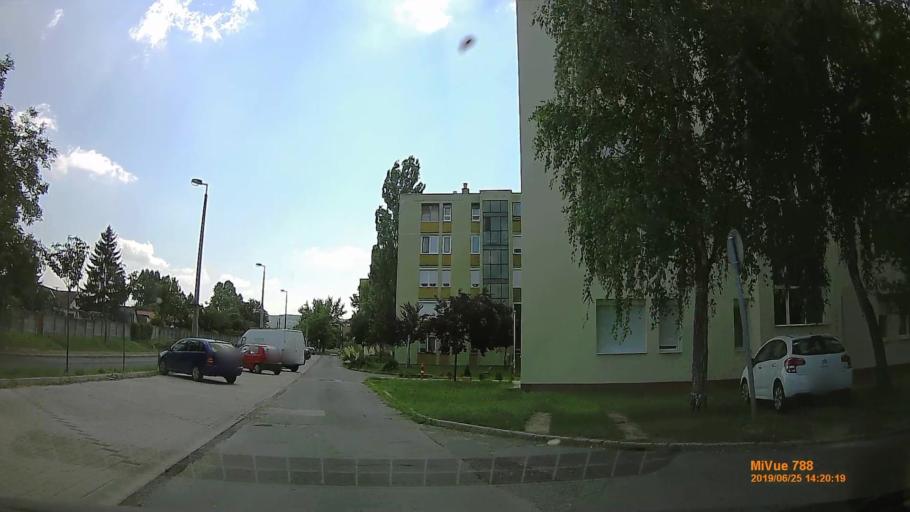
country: HU
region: Komarom-Esztergom
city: Dorog
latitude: 47.7188
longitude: 18.7432
